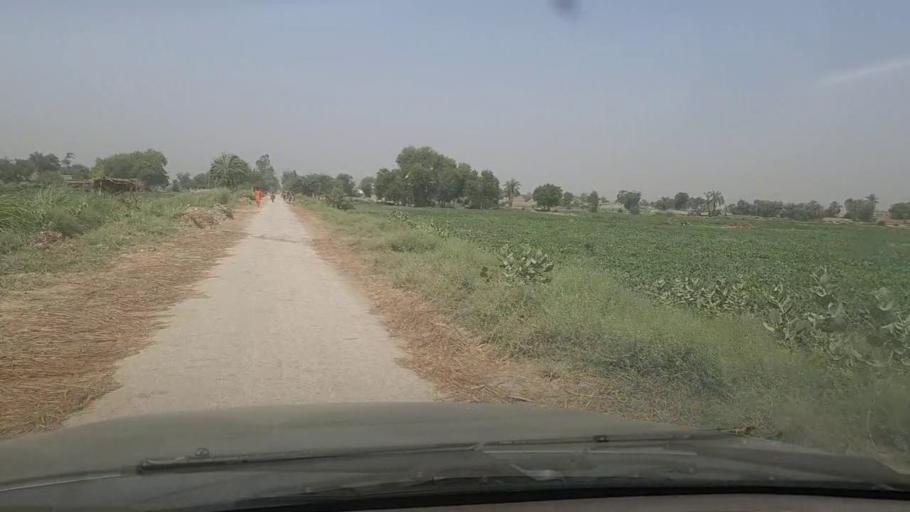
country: PK
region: Sindh
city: Madeji
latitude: 27.7951
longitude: 68.4851
